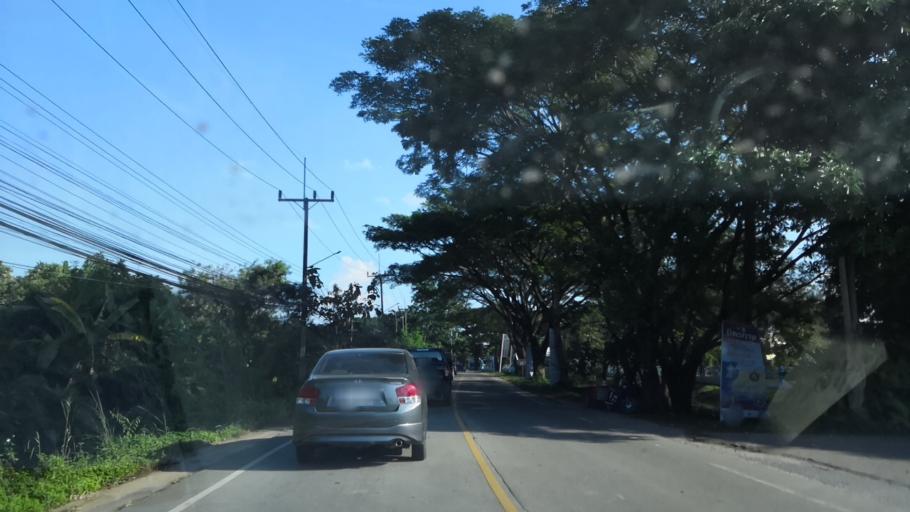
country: TH
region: Chiang Rai
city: Chiang Rai
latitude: 19.9308
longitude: 99.8676
